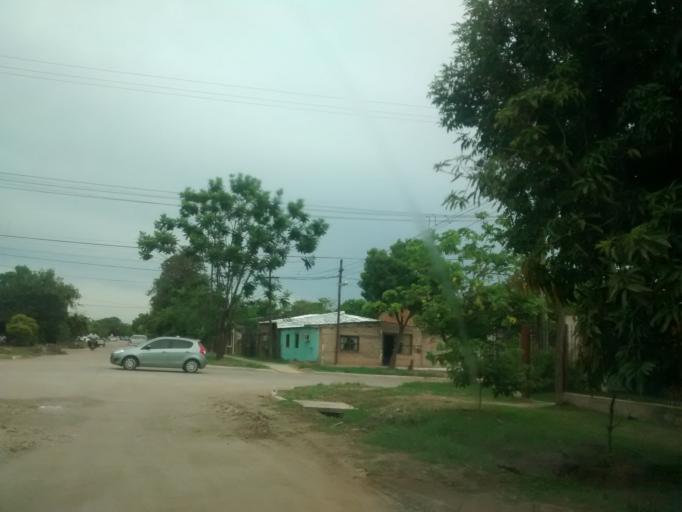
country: AR
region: Chaco
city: Resistencia
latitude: -27.4505
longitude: -59.0109
